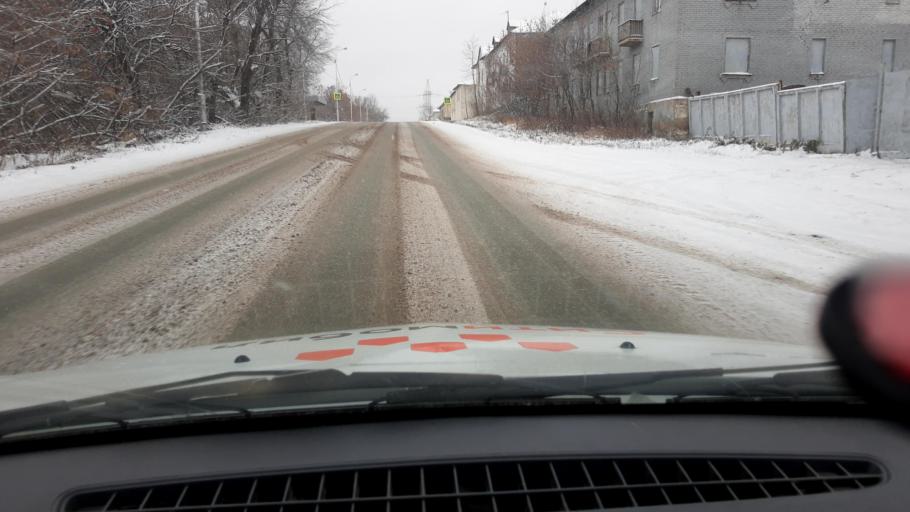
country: RU
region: Bashkortostan
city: Blagoveshchensk
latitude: 54.8991
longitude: 56.0540
